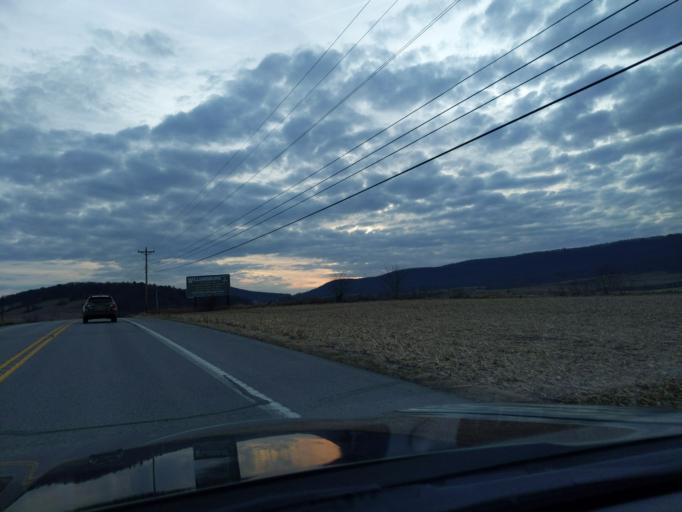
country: US
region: Pennsylvania
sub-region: Blair County
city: Williamsburg
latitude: 40.5227
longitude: -78.2017
